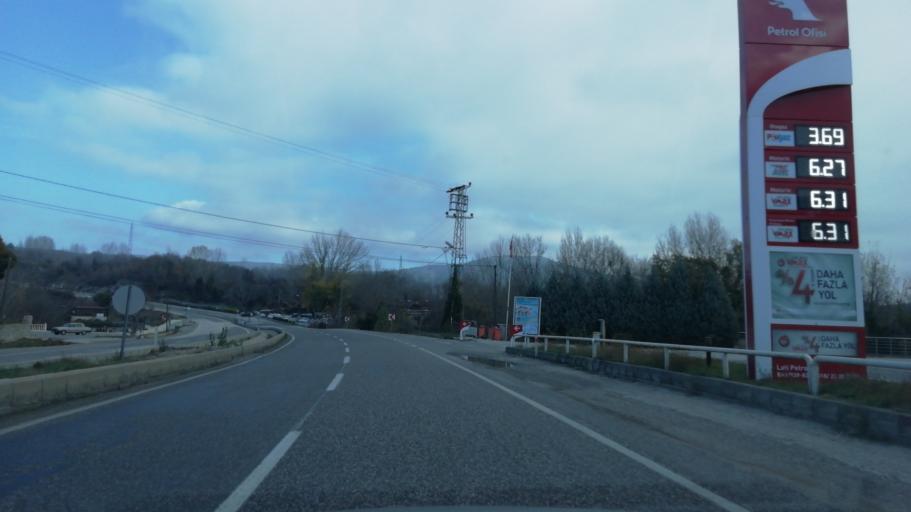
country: TR
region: Karabuk
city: Safranbolu
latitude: 41.2157
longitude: 32.7634
